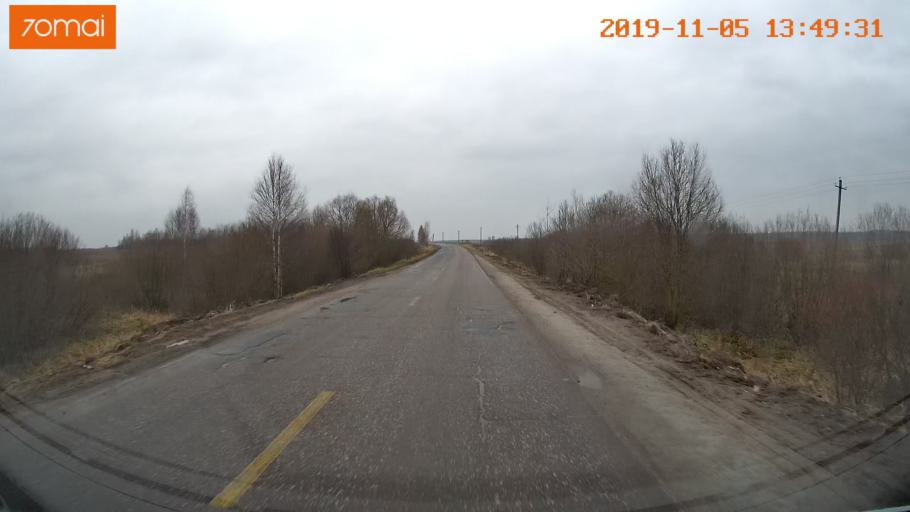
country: RU
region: Ivanovo
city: Kaminskiy
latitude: 57.0112
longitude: 41.4099
